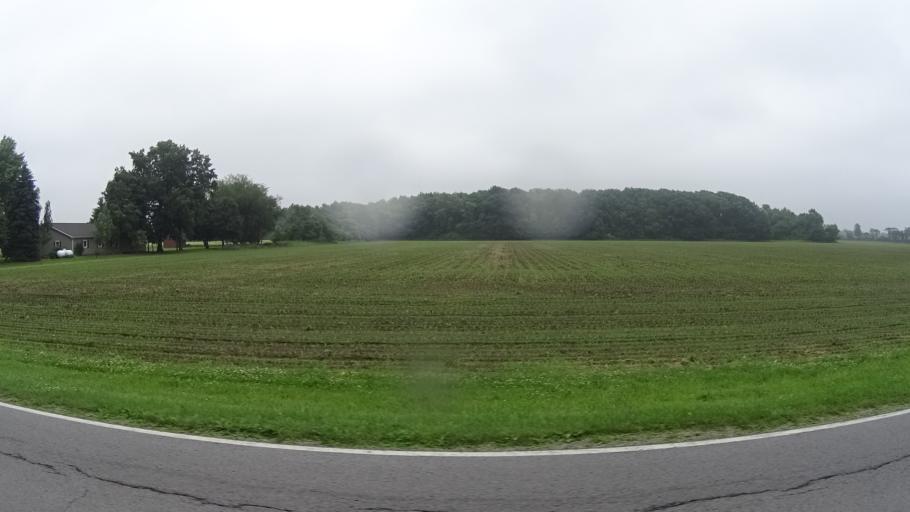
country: US
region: Ohio
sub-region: Huron County
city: Bellevue
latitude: 41.3042
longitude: -82.8421
